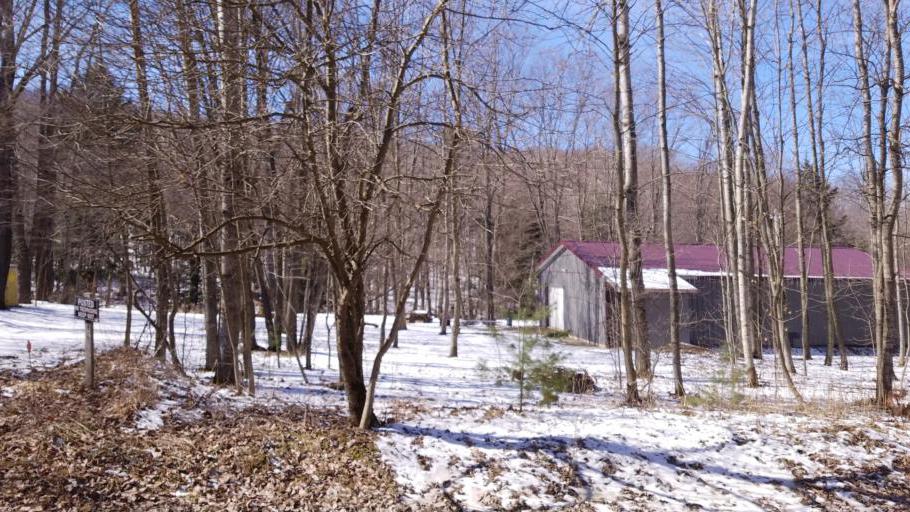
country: US
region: Pennsylvania
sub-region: Tioga County
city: Westfield
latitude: 41.9300
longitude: -77.7314
